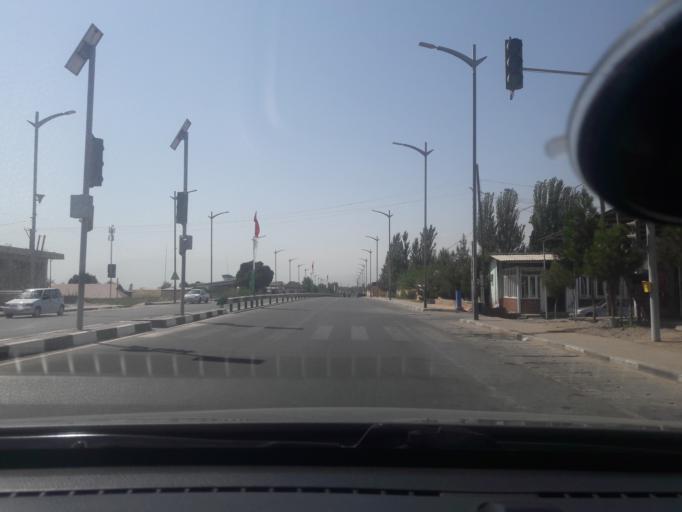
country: TJ
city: Shahrinav
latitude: 38.5622
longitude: 68.4213
